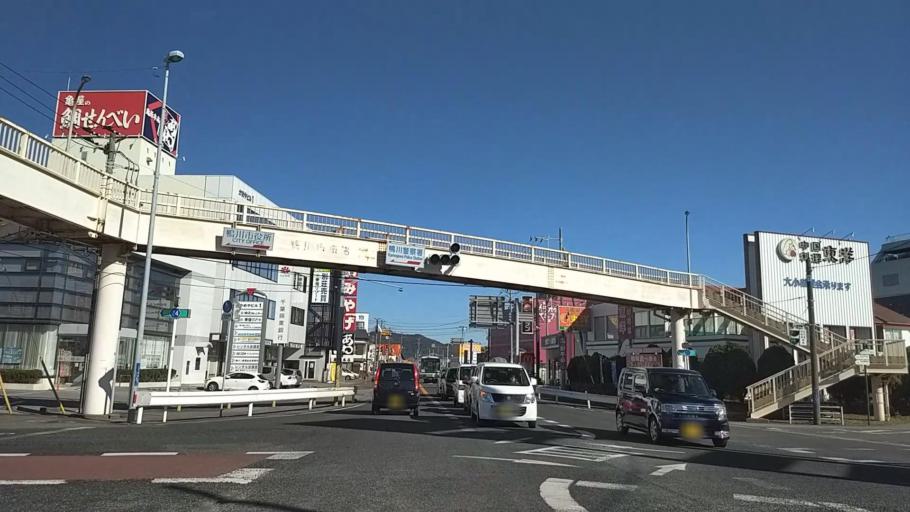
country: JP
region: Chiba
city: Kawaguchi
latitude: 35.1090
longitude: 140.1012
